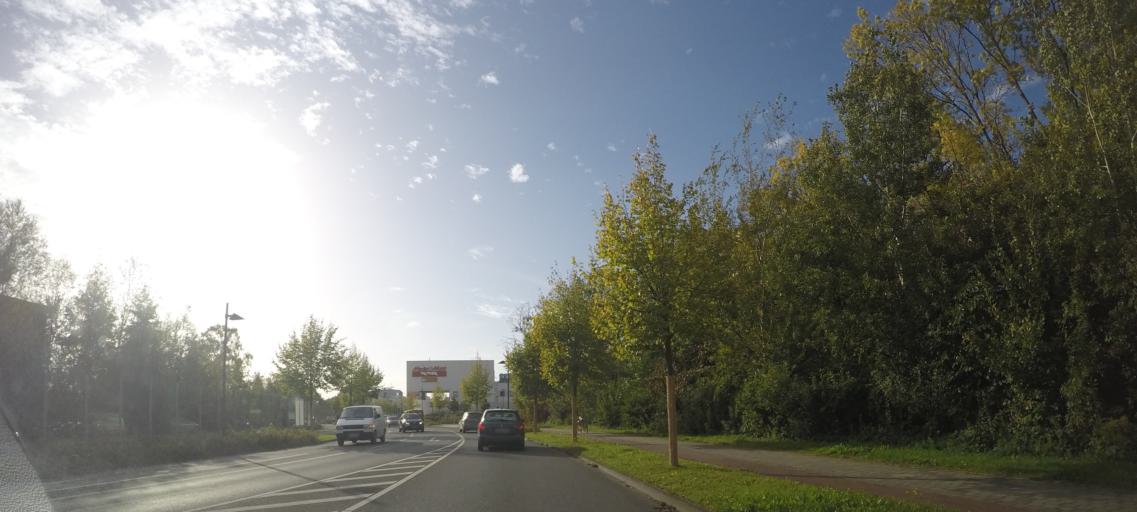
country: DE
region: North Rhine-Westphalia
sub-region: Regierungsbezirk Arnsberg
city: Lippstadt
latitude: 51.6702
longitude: 8.3506
